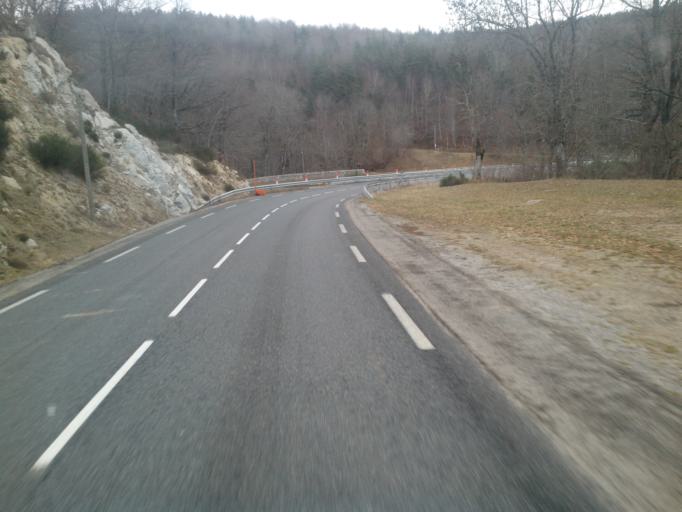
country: FR
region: Languedoc-Roussillon
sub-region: Departement de la Lozere
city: Mende
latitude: 44.5804
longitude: 3.4955
